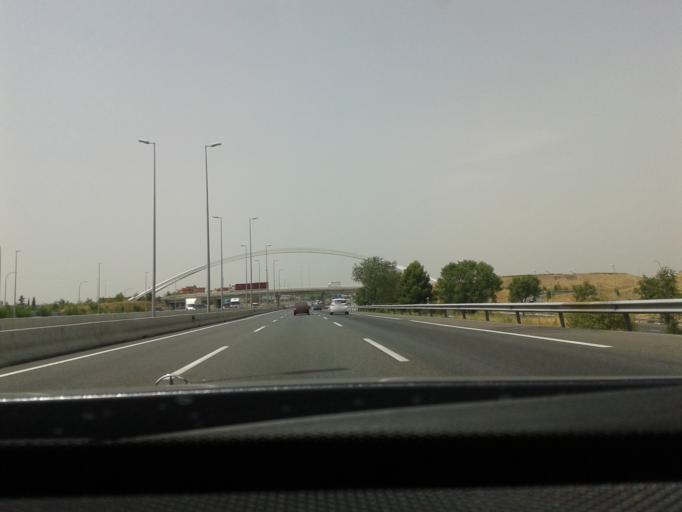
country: ES
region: Madrid
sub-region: Provincia de Madrid
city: Torrejon de Ardoz
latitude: 40.4686
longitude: -3.4365
